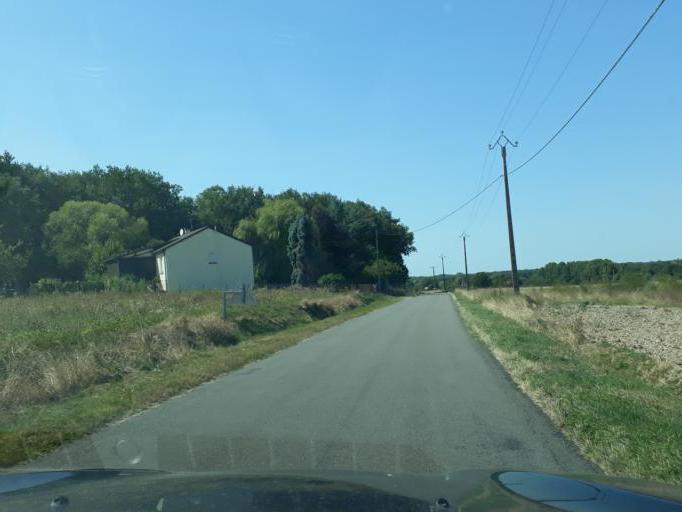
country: FR
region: Centre
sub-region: Departement du Loir-et-Cher
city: Gievres
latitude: 47.2584
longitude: 1.6944
